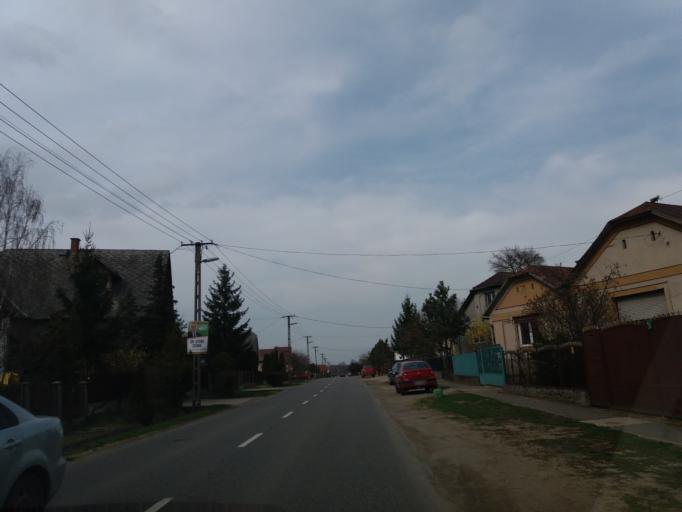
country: HU
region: Szabolcs-Szatmar-Bereg
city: Anarcs
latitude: 48.1777
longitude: 22.1003
